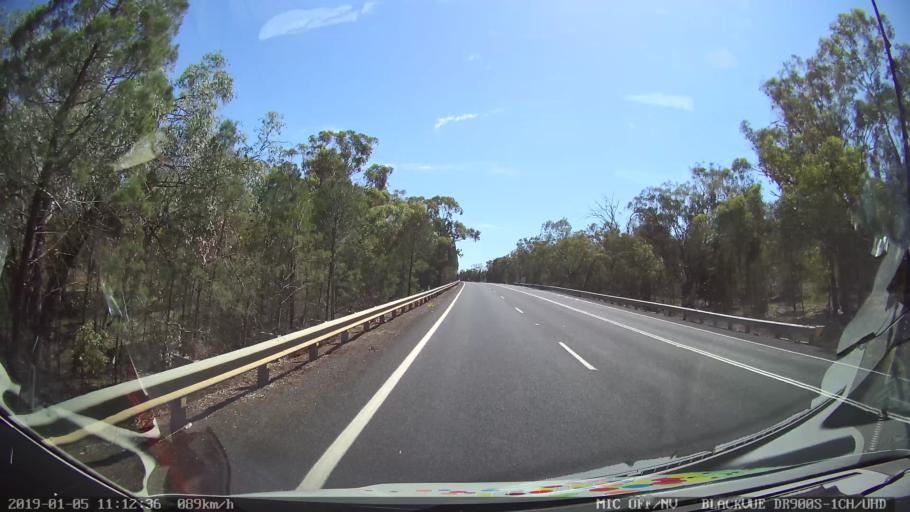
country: AU
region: New South Wales
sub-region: Warrumbungle Shire
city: Coonabarabran
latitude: -31.3804
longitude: 149.2625
